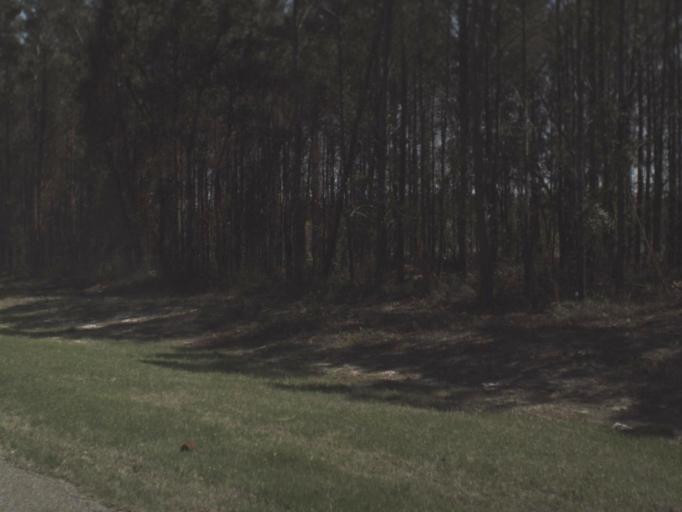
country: US
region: Florida
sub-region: Liberty County
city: Bristol
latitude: 30.4105
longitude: -84.8471
